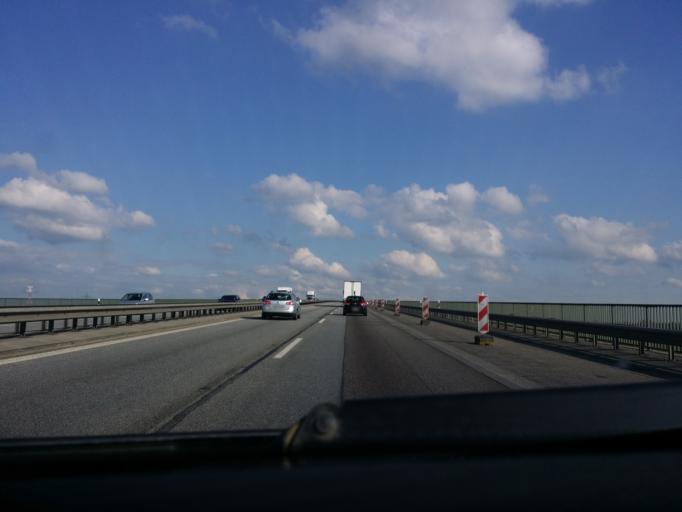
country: DE
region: Schleswig-Holstein
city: Borgstedt
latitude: 54.3357
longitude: 9.7201
